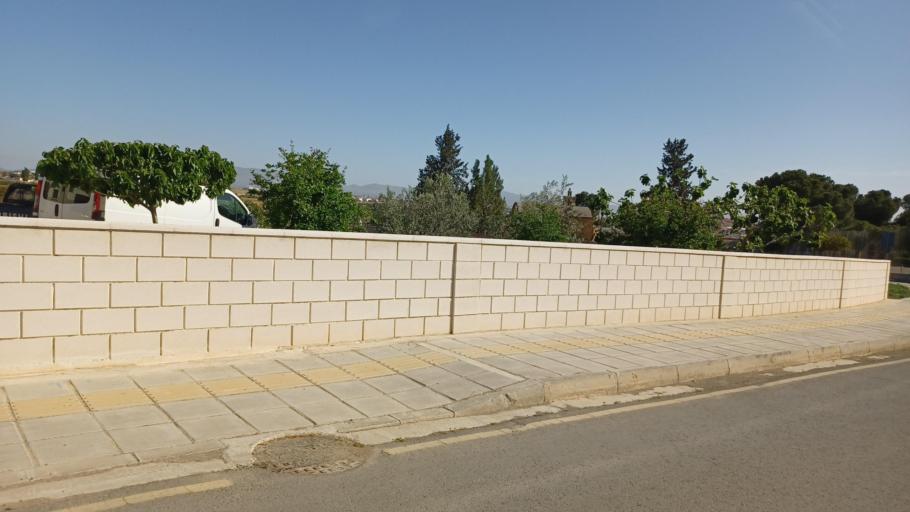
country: CY
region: Lefkosia
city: Kokkinotrimithia
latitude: 35.1527
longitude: 33.1960
